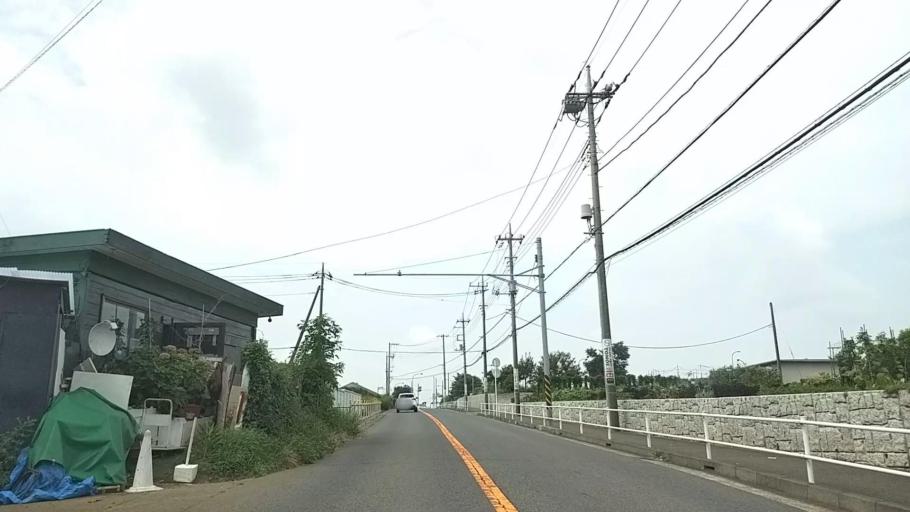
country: JP
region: Kanagawa
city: Yokohama
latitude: 35.5335
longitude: 139.5757
